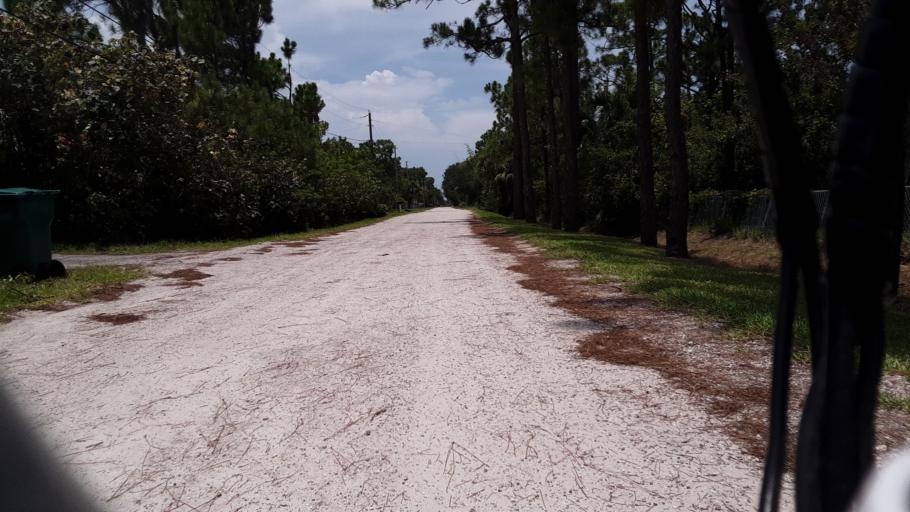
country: US
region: Florida
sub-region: Brevard County
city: Malabar
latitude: 27.9871
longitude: -80.5978
